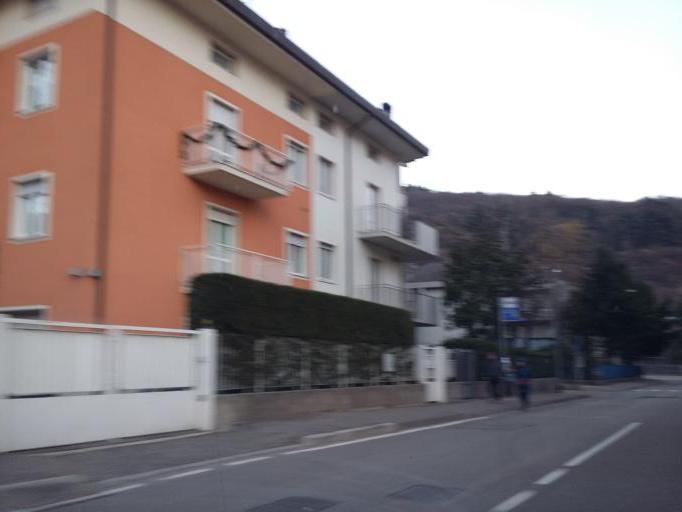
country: IT
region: Trentino-Alto Adige
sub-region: Provincia di Trento
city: Villa Lagarina
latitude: 45.9060
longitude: 11.0426
